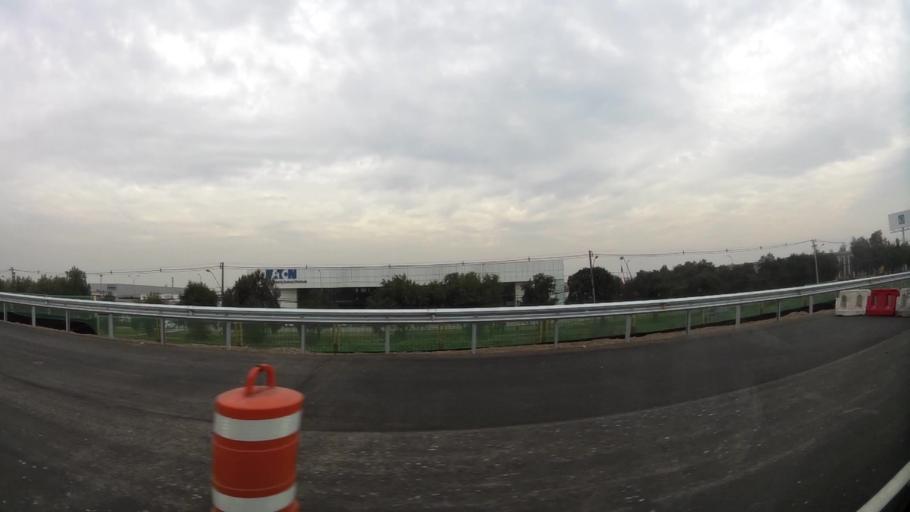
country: CL
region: Santiago Metropolitan
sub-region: Provincia de Chacabuco
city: Chicureo Abajo
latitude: -33.3233
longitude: -70.7194
